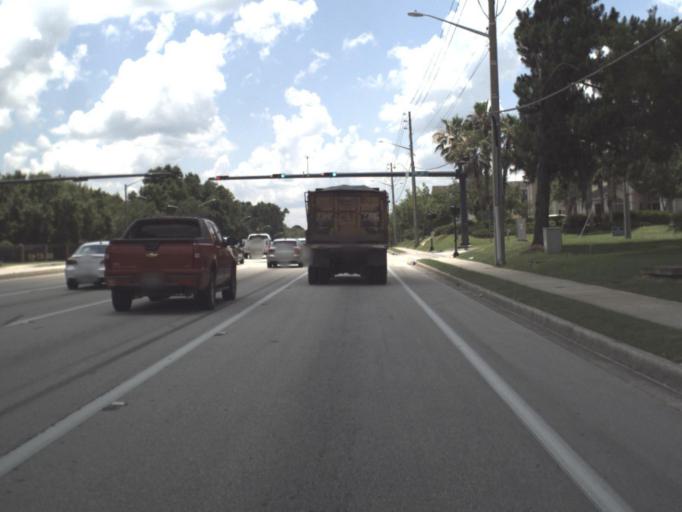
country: US
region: Florida
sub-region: Alachua County
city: Gainesville
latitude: 29.6186
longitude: -82.3727
